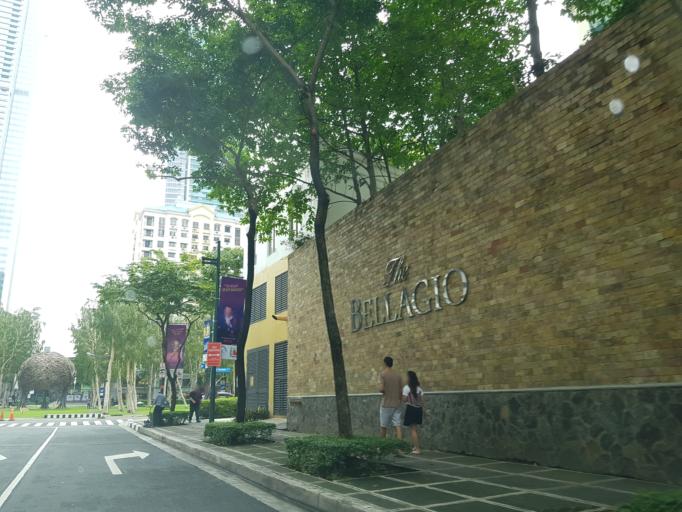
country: PH
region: Metro Manila
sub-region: Makati City
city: Makati City
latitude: 14.5530
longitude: 121.0436
